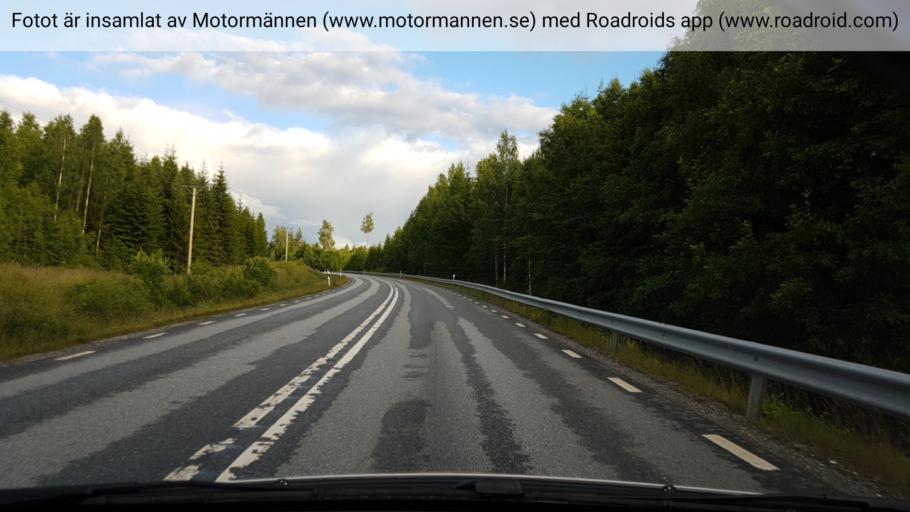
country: SE
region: OErebro
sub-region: Hallefors Kommun
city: Haellefors
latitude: 59.6451
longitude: 14.6008
